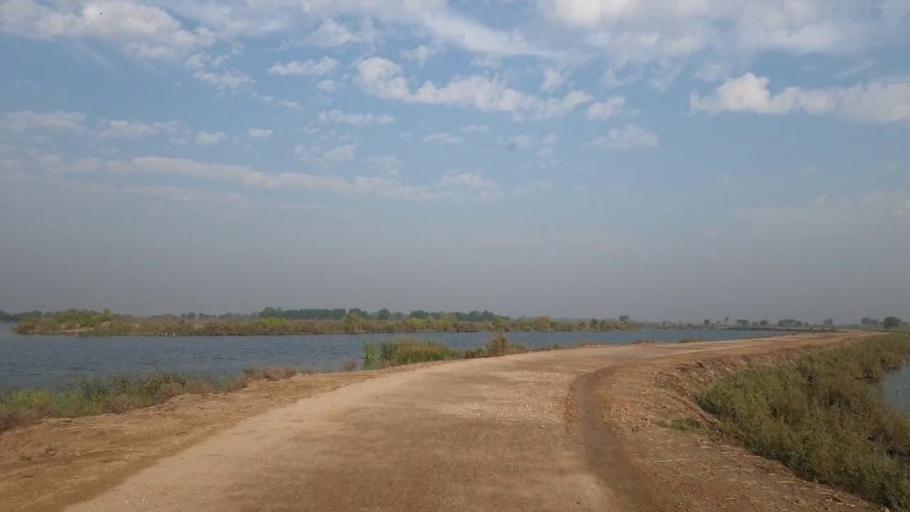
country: PK
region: Sindh
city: Tando Bago
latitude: 24.8124
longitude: 68.9566
